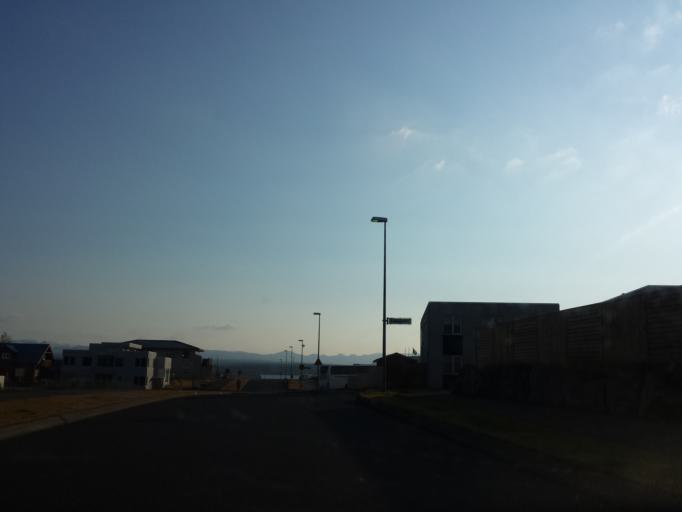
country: IS
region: Capital Region
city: Reykjavik
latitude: 64.0906
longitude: -21.8050
